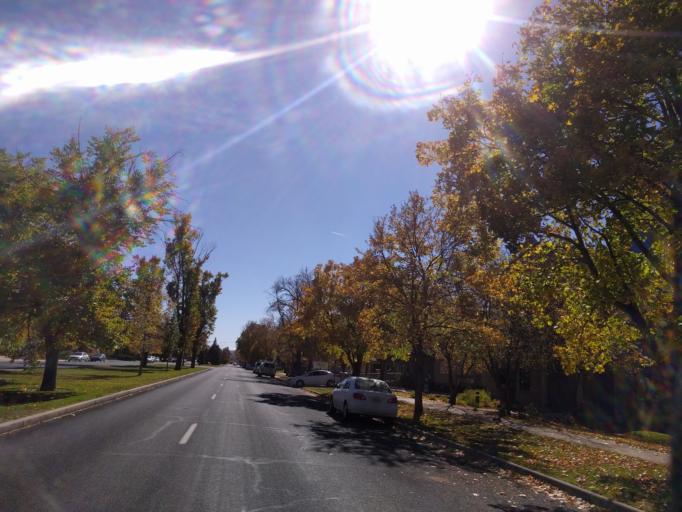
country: US
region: Colorado
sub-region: El Paso County
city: Colorado Springs
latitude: 38.8421
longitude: -104.8250
